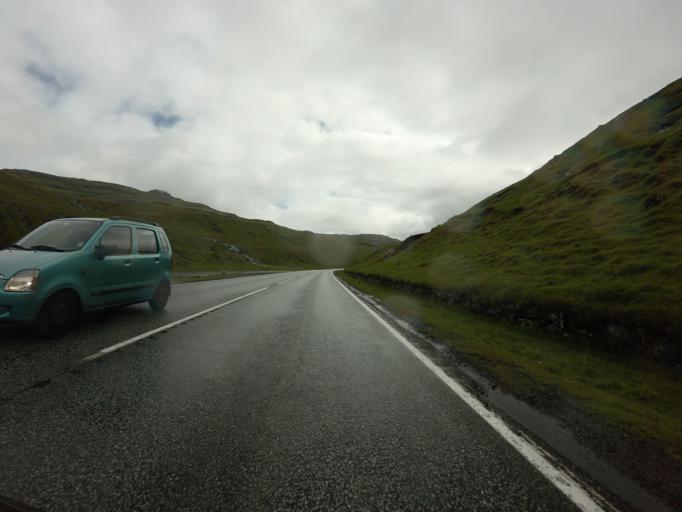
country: FO
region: Streymoy
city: Kollafjordhur
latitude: 62.1278
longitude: -7.0074
